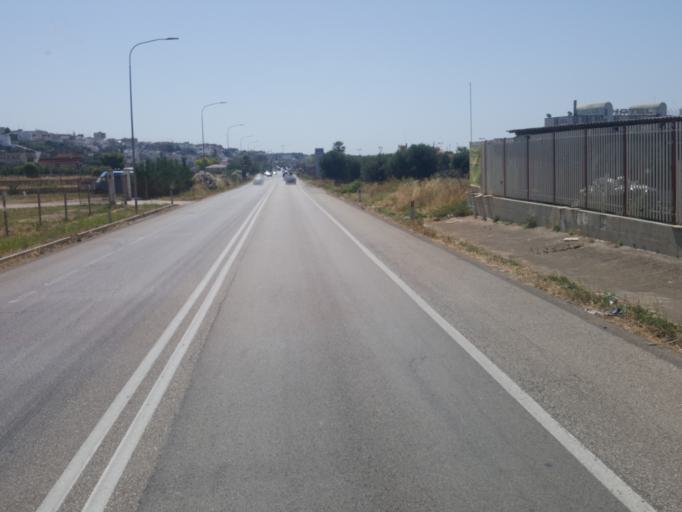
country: IT
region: Apulia
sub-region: Provincia di Taranto
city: Massafra
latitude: 40.5903
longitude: 17.0987
